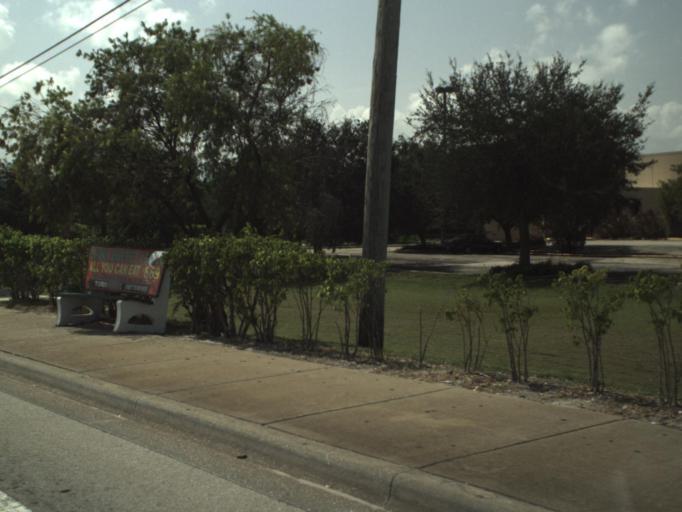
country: US
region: Florida
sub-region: Palm Beach County
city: Boca Pointe
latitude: 26.3180
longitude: -80.1538
